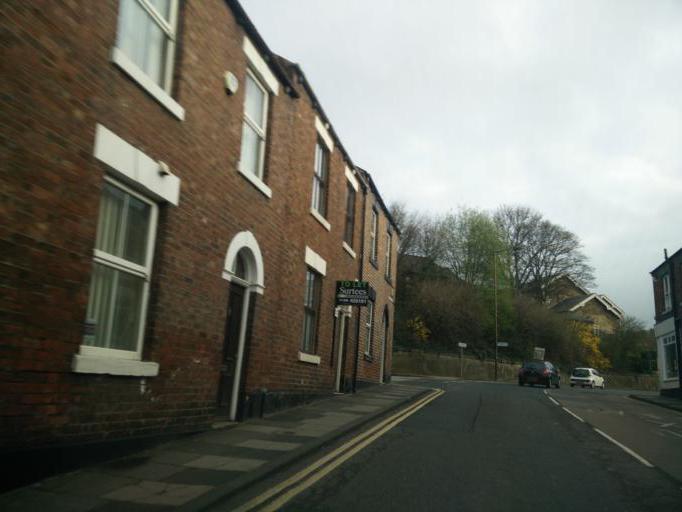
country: GB
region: England
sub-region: County Durham
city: Durham
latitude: 54.7765
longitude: -1.5848
